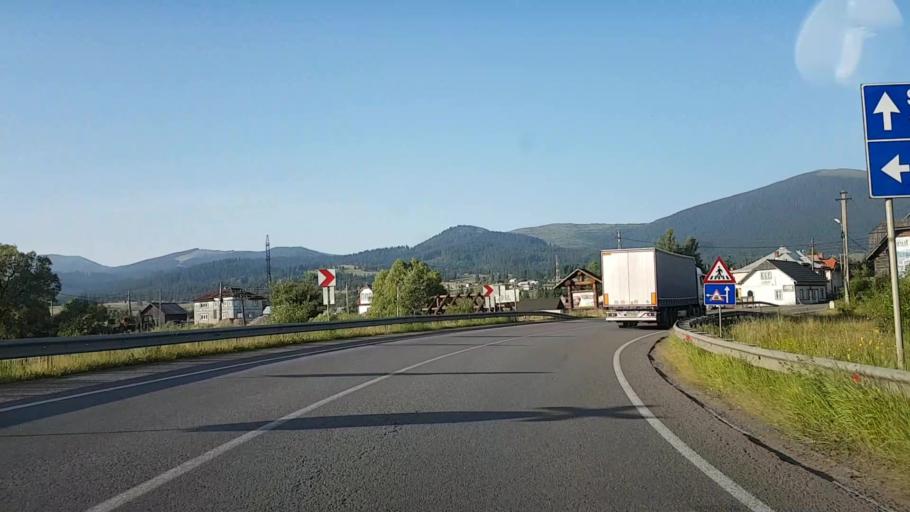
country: RO
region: Suceava
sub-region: Comuna Cosna
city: Cosna
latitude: 47.3606
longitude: 25.1904
